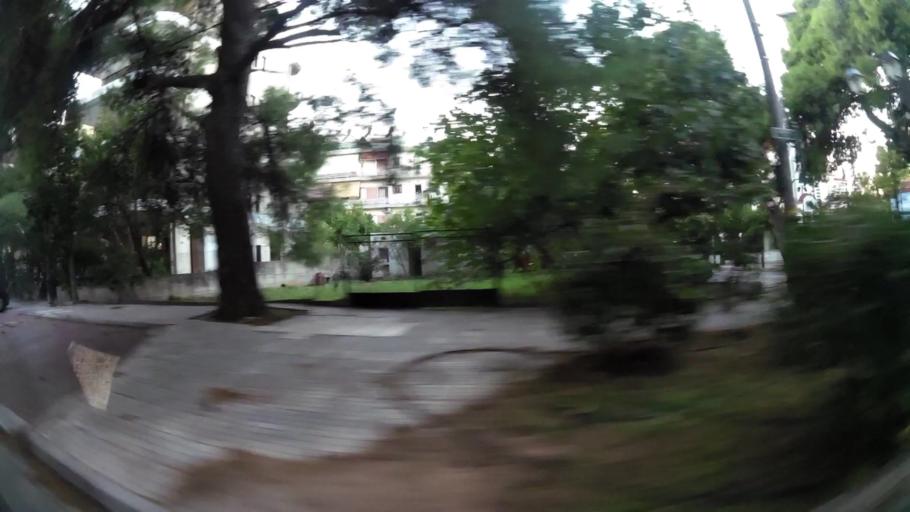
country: GR
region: Attica
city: Pefki
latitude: 38.0639
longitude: 23.7975
